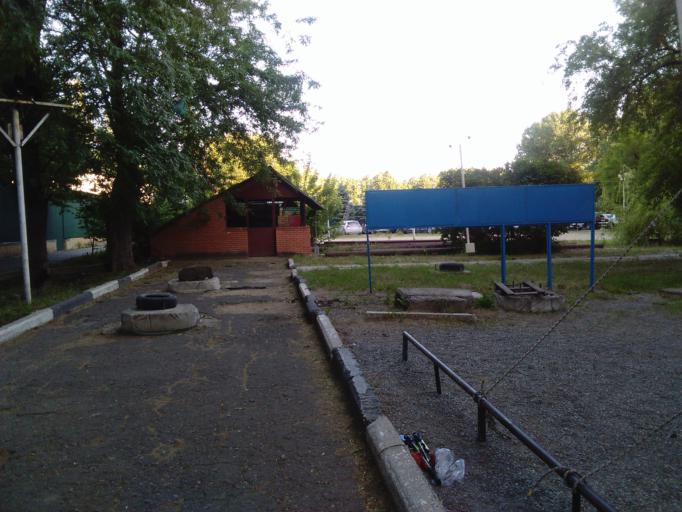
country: RU
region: Rostov
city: Imeni Chkalova
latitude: 47.2458
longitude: 39.7578
